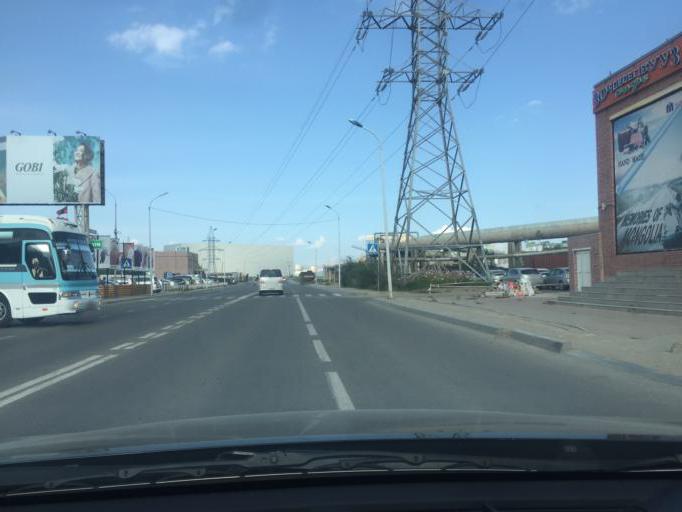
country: MN
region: Ulaanbaatar
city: Ulaanbaatar
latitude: 47.9014
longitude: 106.8676
